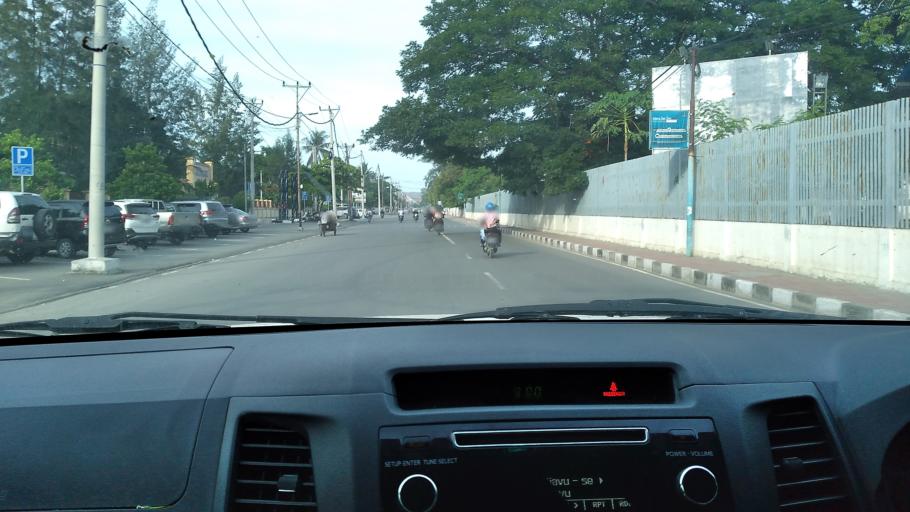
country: TL
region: Dili
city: Dili
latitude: -8.5564
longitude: 125.5785
